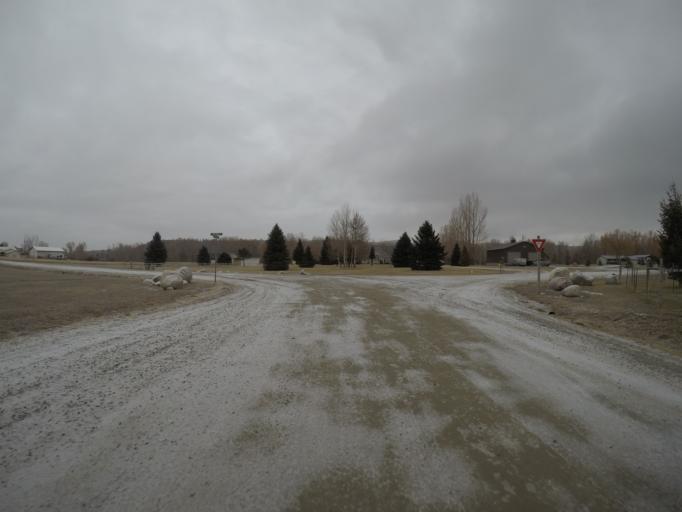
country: US
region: Montana
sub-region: Stillwater County
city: Absarokee
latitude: 45.5295
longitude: -109.4471
